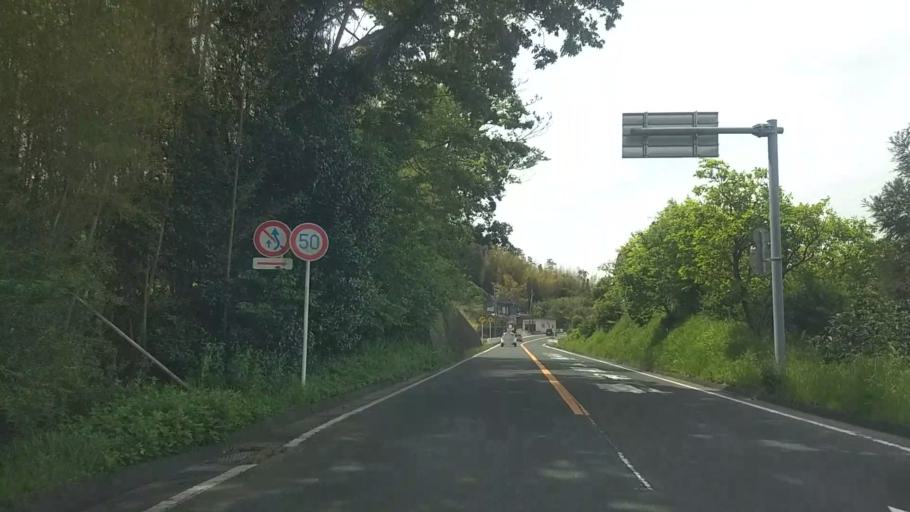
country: JP
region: Shizuoka
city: Kosai-shi
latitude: 34.7893
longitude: 137.5827
